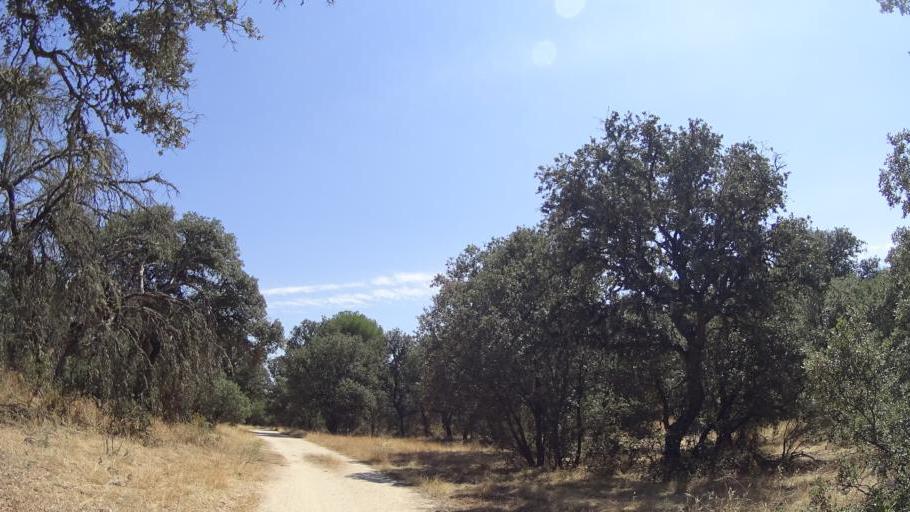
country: ES
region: Madrid
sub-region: Provincia de Madrid
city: Boadilla del Monte
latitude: 40.4250
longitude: -3.8587
